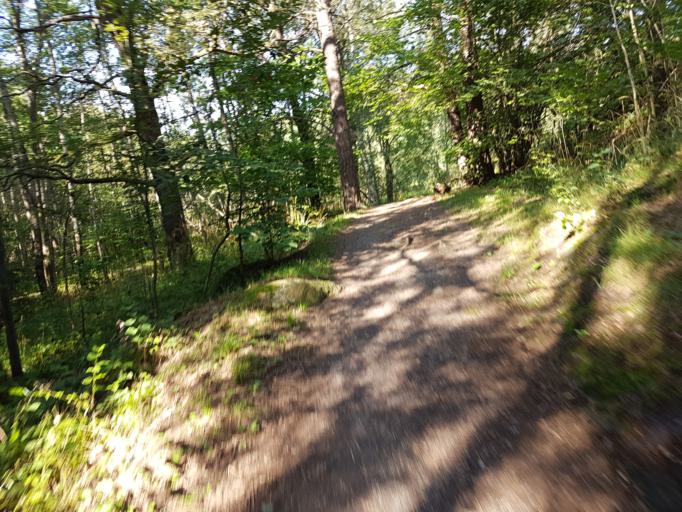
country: SE
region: Stockholm
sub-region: Huddinge Kommun
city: Huddinge
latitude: 59.2648
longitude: 17.9998
